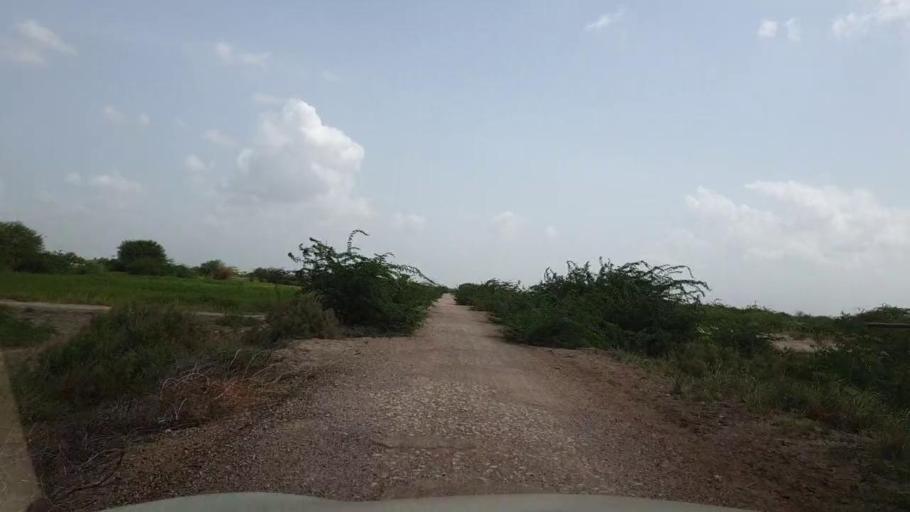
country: PK
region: Sindh
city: Kadhan
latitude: 24.3971
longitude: 68.7967
